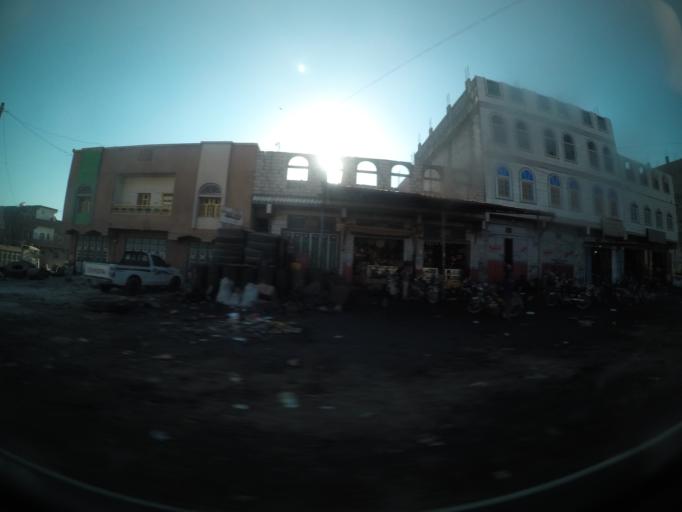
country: YE
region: Lahij
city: Habil ar Raydah
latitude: 13.6413
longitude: 44.8581
